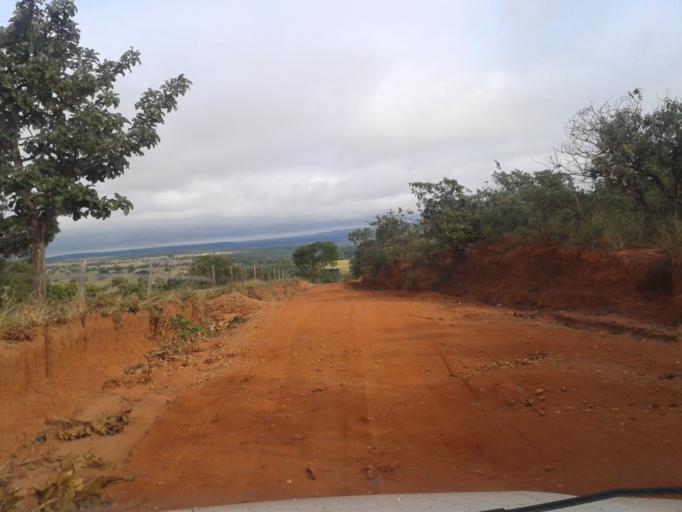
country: BR
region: Minas Gerais
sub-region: Campina Verde
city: Campina Verde
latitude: -19.4032
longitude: -49.6289
